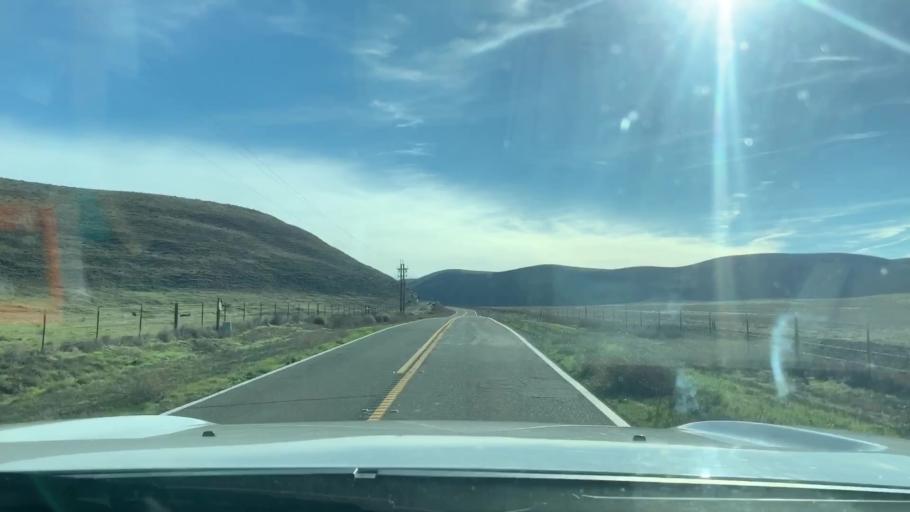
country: US
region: California
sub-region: Monterey County
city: King City
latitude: 36.1535
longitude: -120.9736
